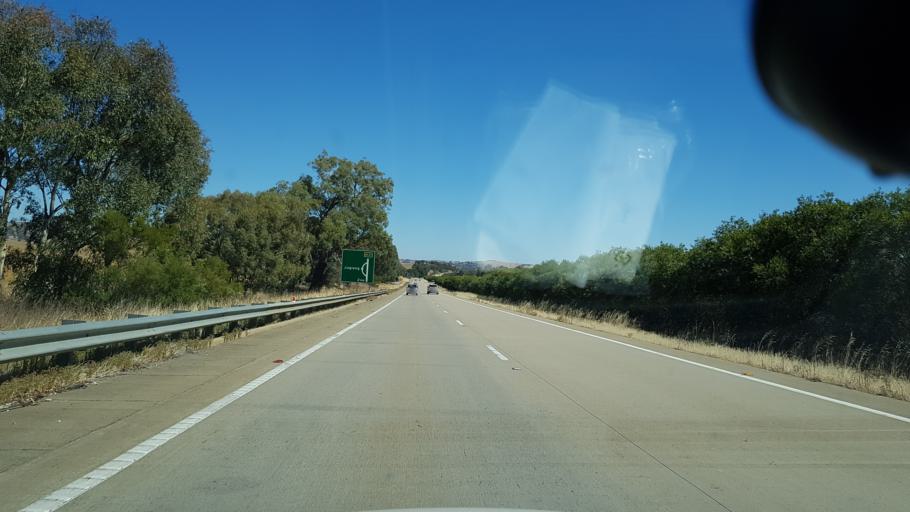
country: AU
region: New South Wales
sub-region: Gundagai
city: Gundagai
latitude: -34.8178
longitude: 148.3867
